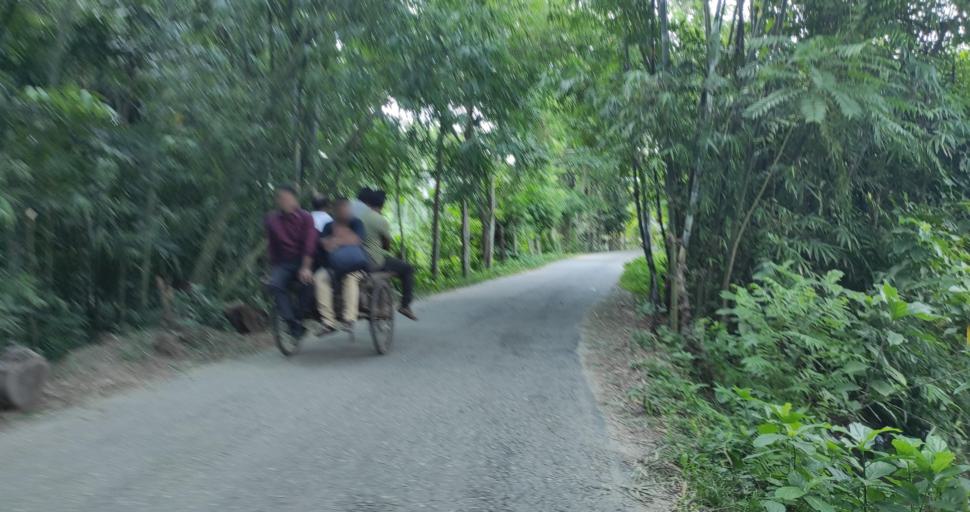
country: BD
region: Barisal
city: Gaurnadi
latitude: 22.8976
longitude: 90.1832
